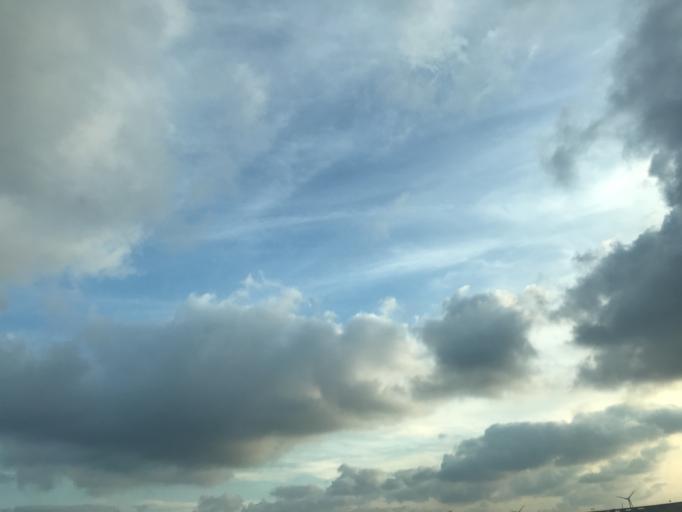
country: TR
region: Istanbul
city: Durusu
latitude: 41.2616
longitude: 28.7136
